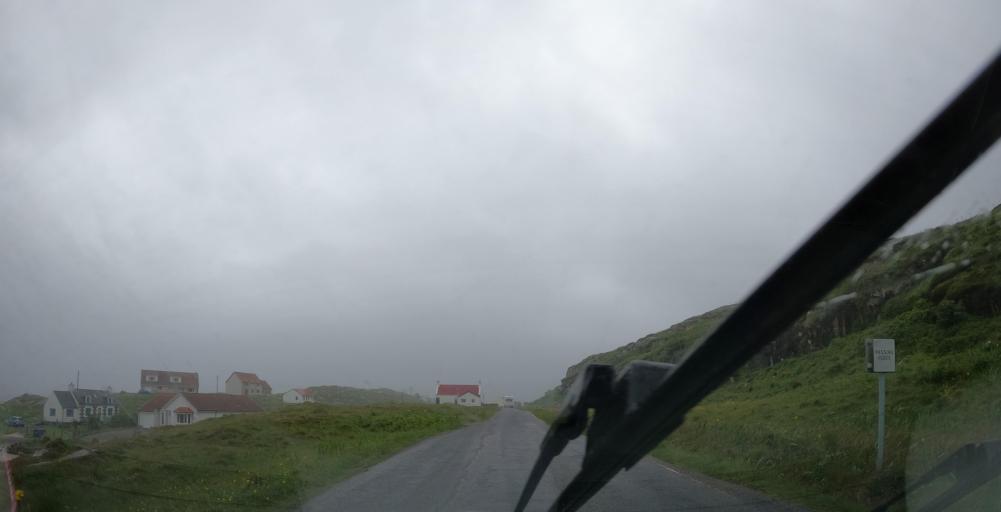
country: GB
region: Scotland
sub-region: Eilean Siar
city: Barra
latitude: 57.0149
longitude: -7.4322
